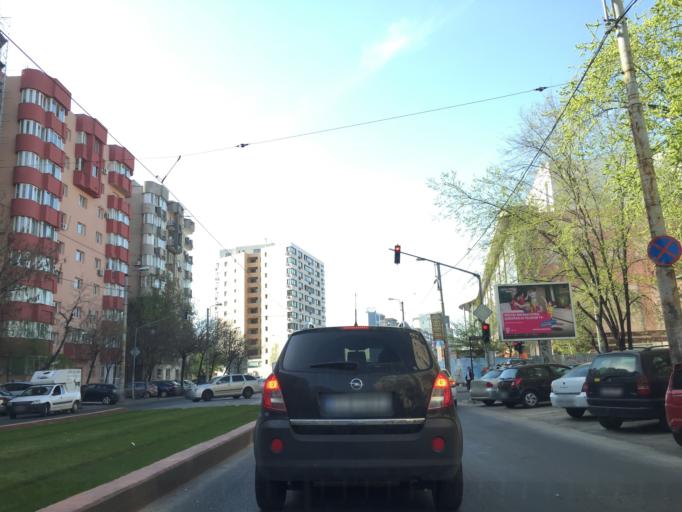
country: RO
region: Bucuresti
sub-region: Municipiul Bucuresti
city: Bucharest
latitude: 44.4189
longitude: 26.1273
